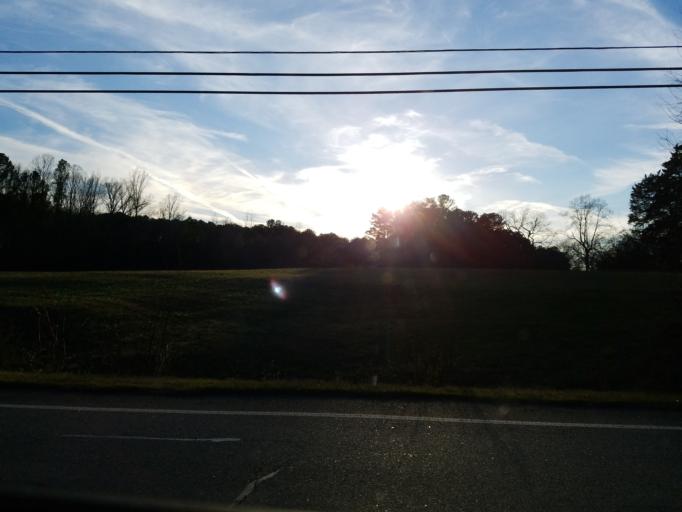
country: US
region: Georgia
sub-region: Whitfield County
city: Dalton
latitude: 34.6417
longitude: -84.9669
